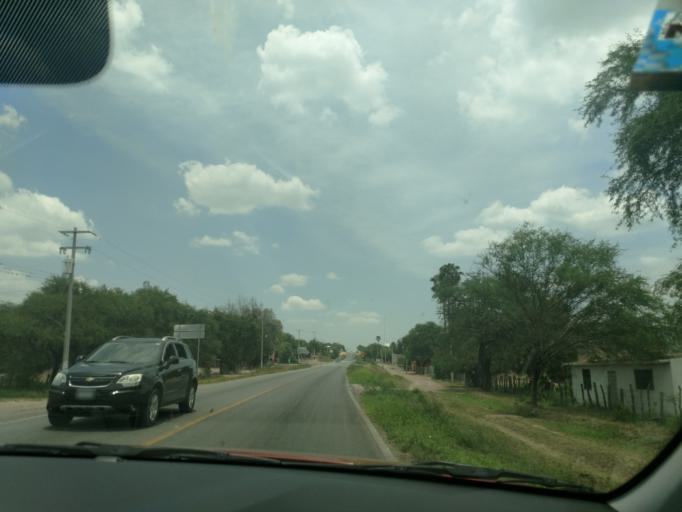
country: MX
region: San Luis Potosi
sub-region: Rioverde
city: Progreso
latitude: 22.0194
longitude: -100.3778
